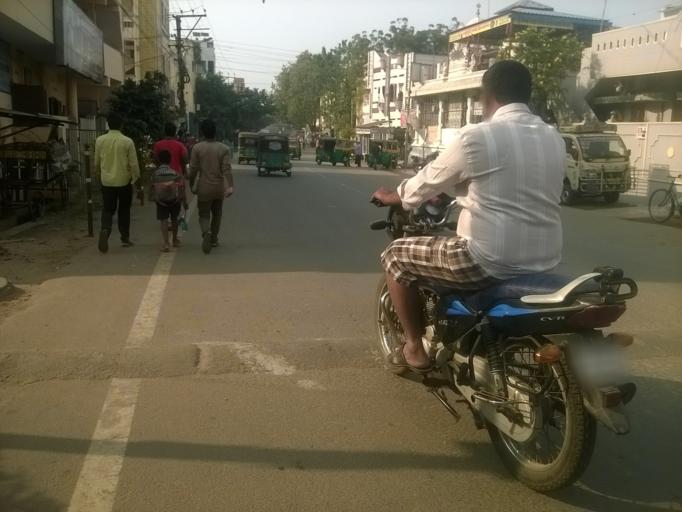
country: IN
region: Andhra Pradesh
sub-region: Krishna
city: Vijayawada
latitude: 16.5234
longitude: 80.6041
